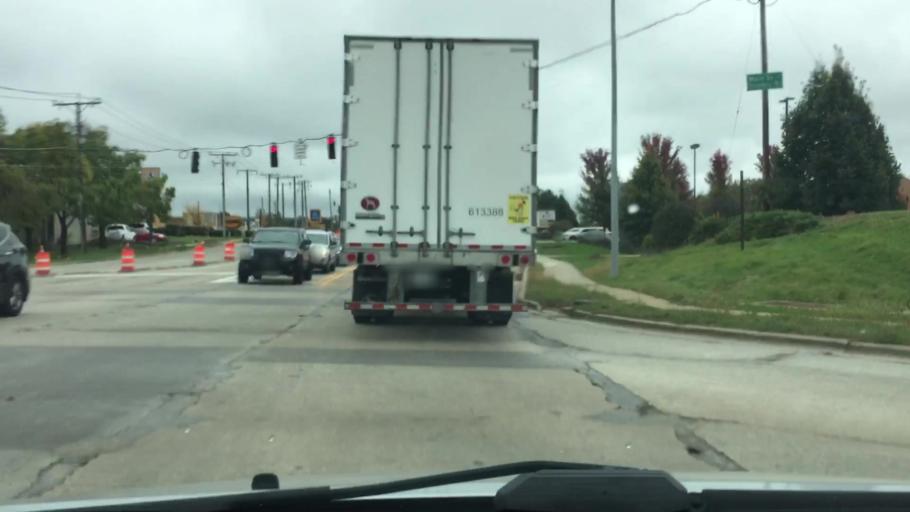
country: US
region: Illinois
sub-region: Kane County
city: West Dundee
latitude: 42.1078
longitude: -88.2937
